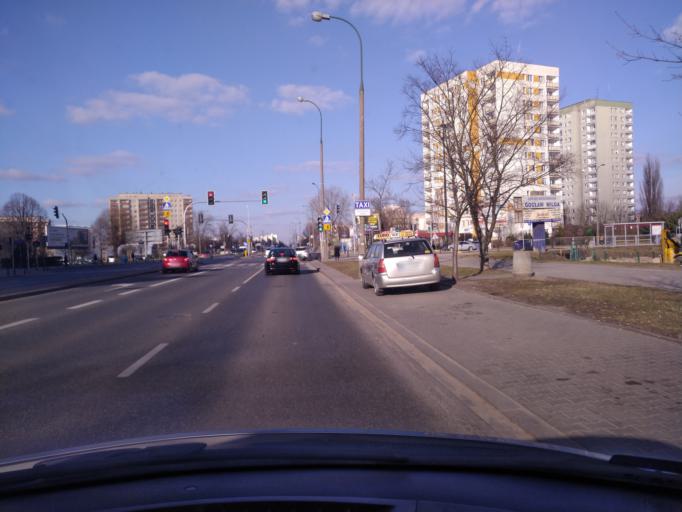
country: PL
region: Masovian Voivodeship
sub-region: Warszawa
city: Praga Poludnie
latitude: 52.2269
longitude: 21.0937
